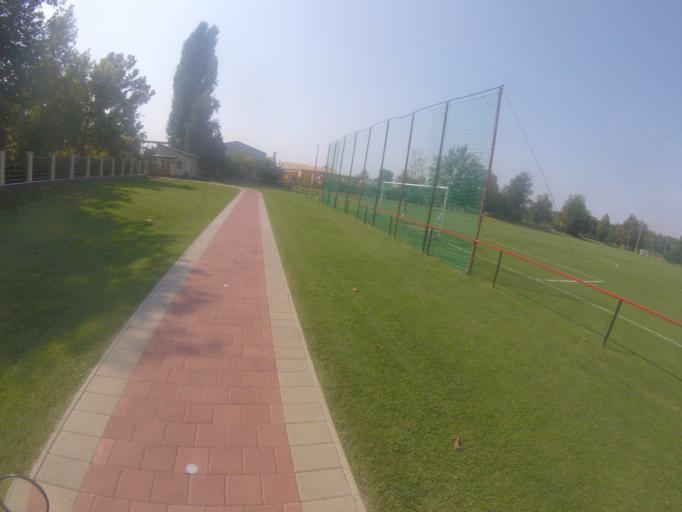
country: HU
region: Bacs-Kiskun
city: Ersekcsanad
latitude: 46.2496
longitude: 18.9759
